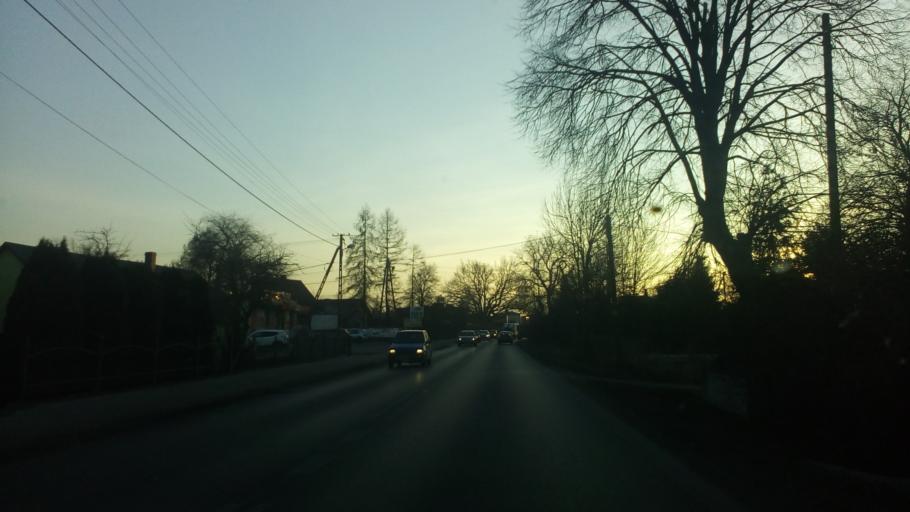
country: PL
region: Lesser Poland Voivodeship
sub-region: Powiat nowosadecki
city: Chelmiec
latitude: 49.6094
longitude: 20.6574
